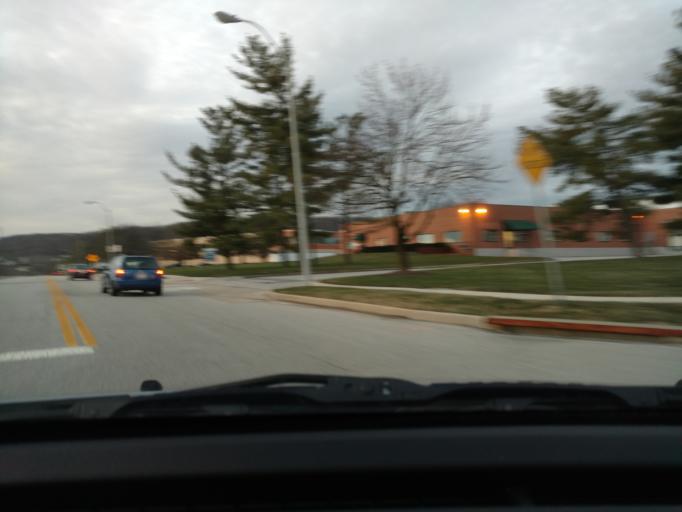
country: US
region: Maryland
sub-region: Baltimore County
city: Cockeysville
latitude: 39.4815
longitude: -76.6620
